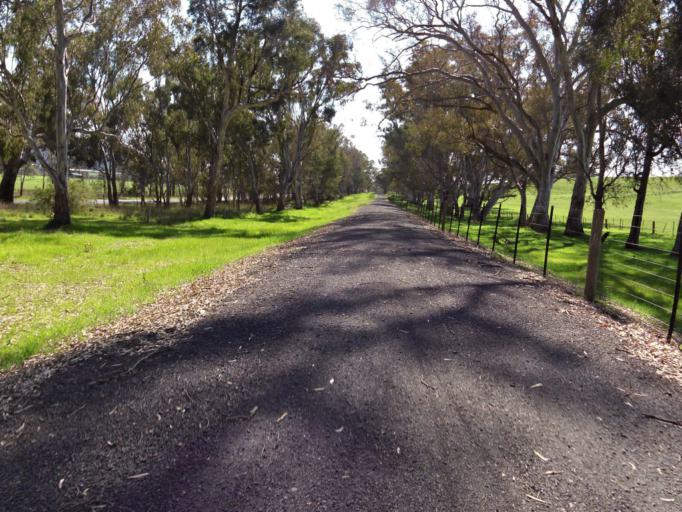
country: AU
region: Victoria
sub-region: Murrindindi
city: Alexandra
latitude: -37.1390
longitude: 145.5905
